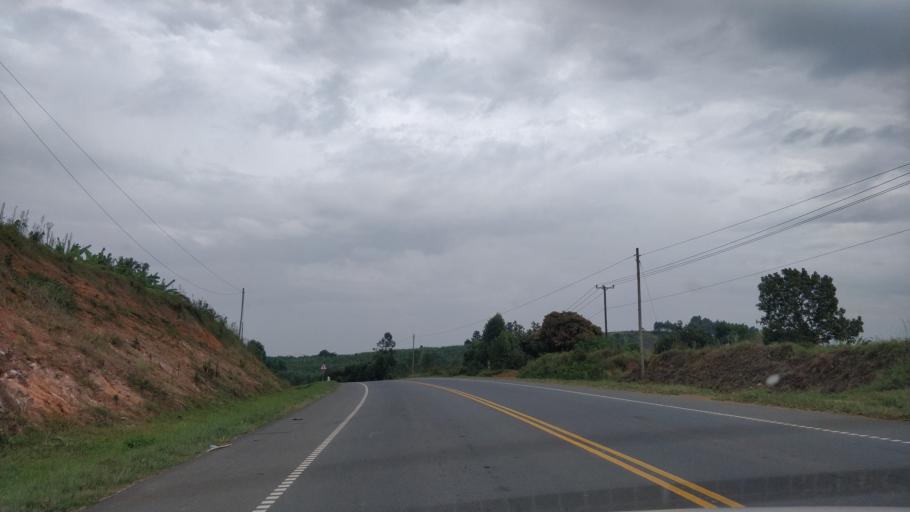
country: UG
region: Western Region
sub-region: Sheema District
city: Kibingo
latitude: -0.6551
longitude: 30.4816
